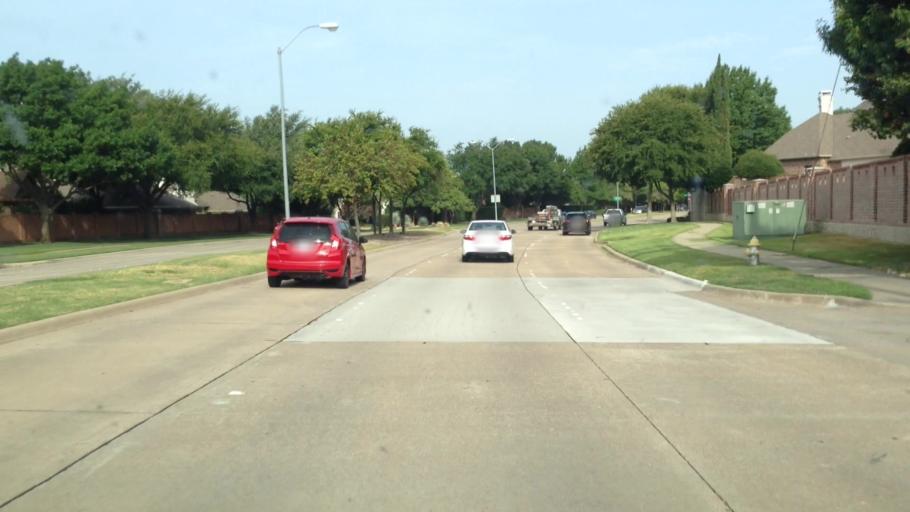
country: US
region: Texas
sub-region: Denton County
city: The Colony
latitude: 33.0453
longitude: -96.8412
